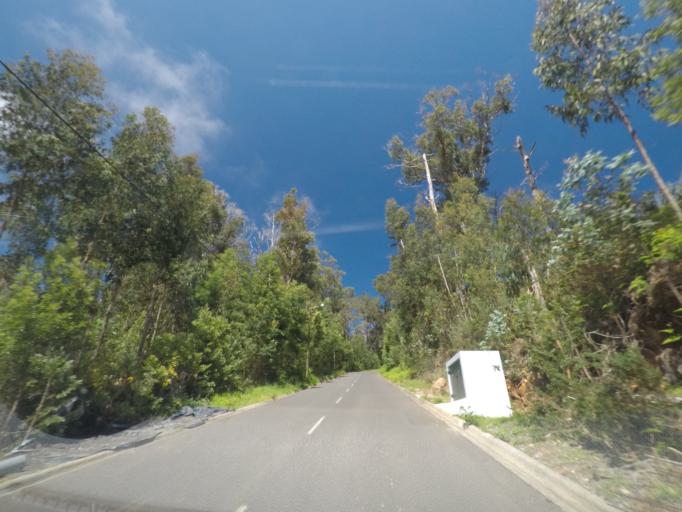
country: PT
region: Madeira
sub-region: Calheta
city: Arco da Calheta
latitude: 32.7301
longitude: -17.1334
